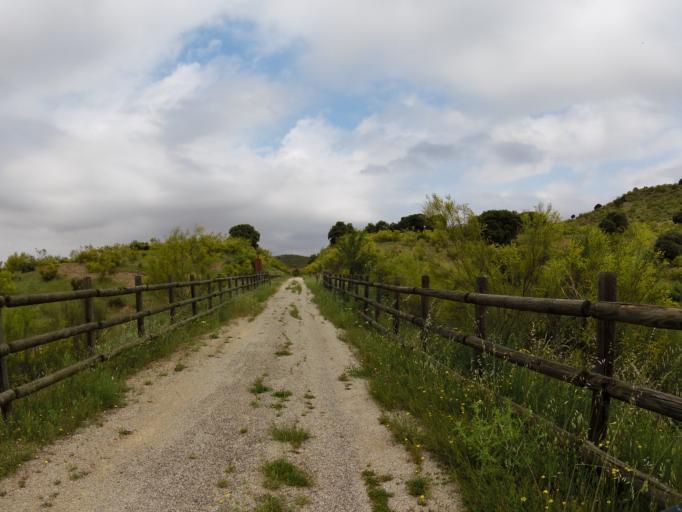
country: ES
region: Castille-La Mancha
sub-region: Provincia de Albacete
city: Alcaraz
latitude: 38.7033
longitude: -2.4856
